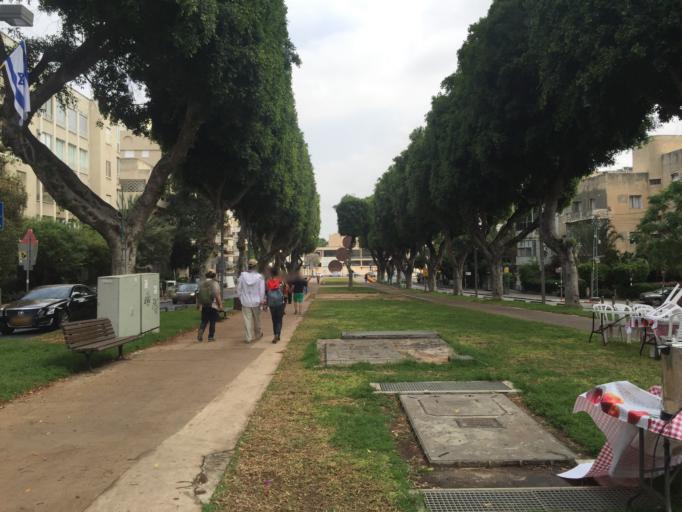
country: IL
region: Tel Aviv
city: Tel Aviv
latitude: 32.0706
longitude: 34.7788
